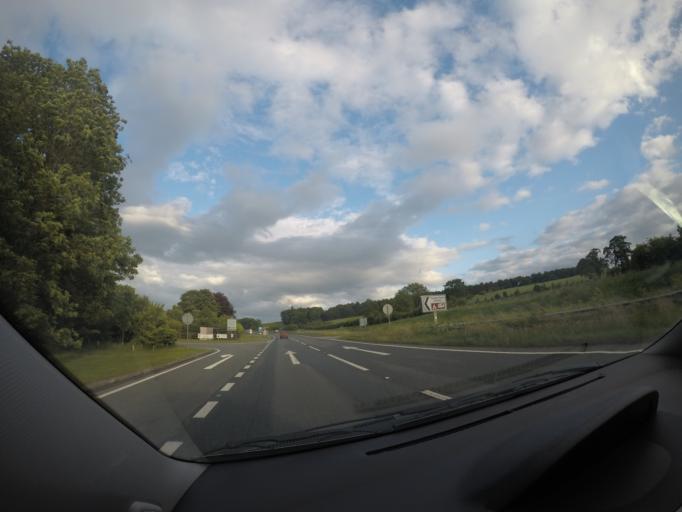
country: GB
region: England
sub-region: County Durham
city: Rokeby
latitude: 54.5111
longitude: -1.8601
